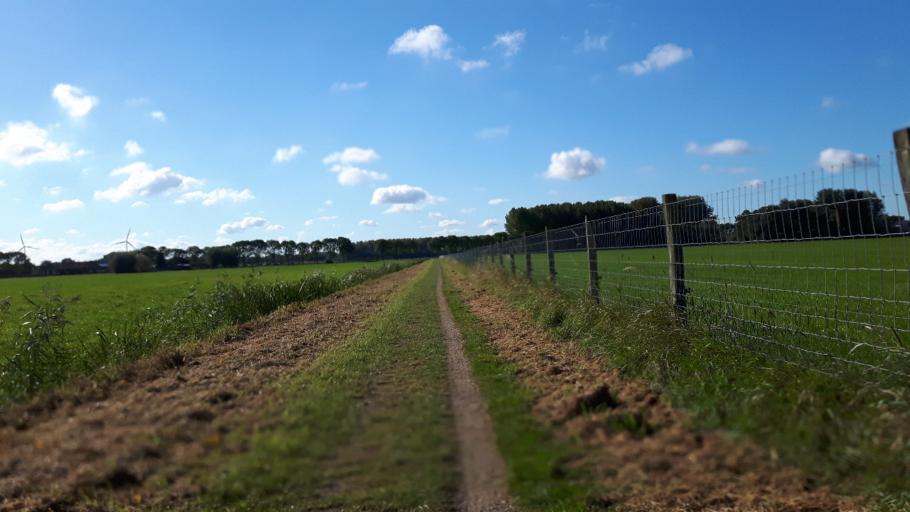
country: NL
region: Gelderland
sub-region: Gemeente Culemborg
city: Culemborg
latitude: 51.9547
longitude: 5.1876
